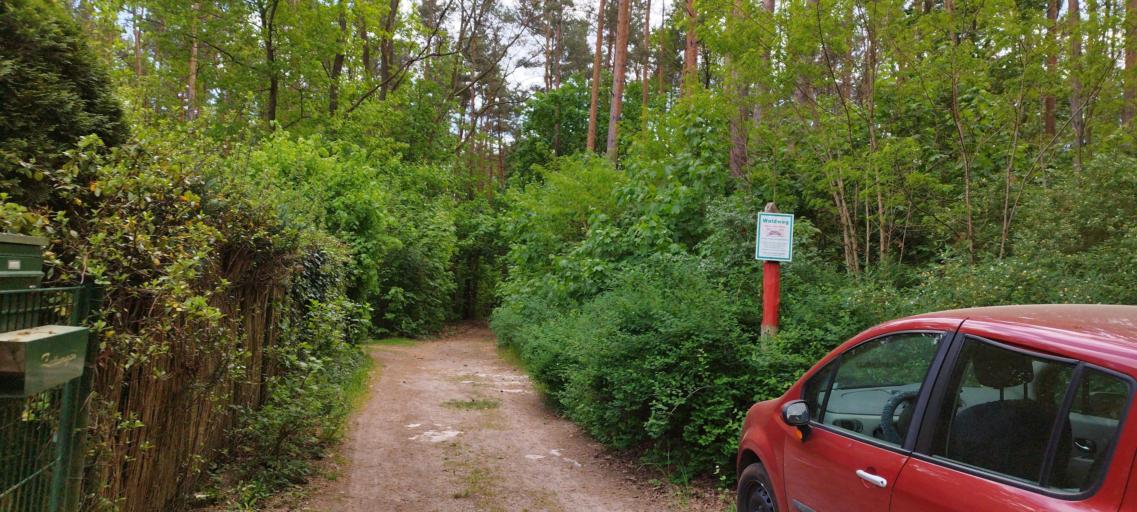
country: DE
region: Brandenburg
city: Grunheide
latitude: 52.4265
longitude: 13.8310
